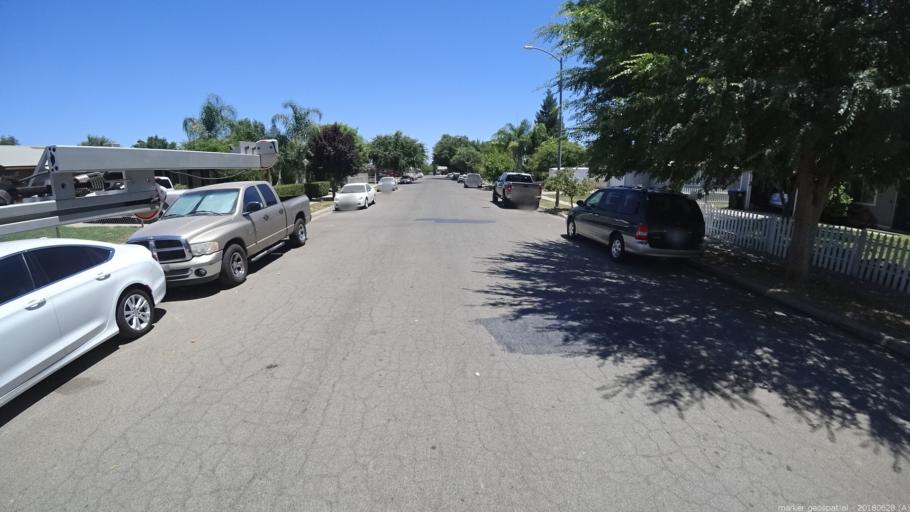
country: US
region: California
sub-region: Madera County
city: Parksdale
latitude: 36.9403
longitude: -120.0261
